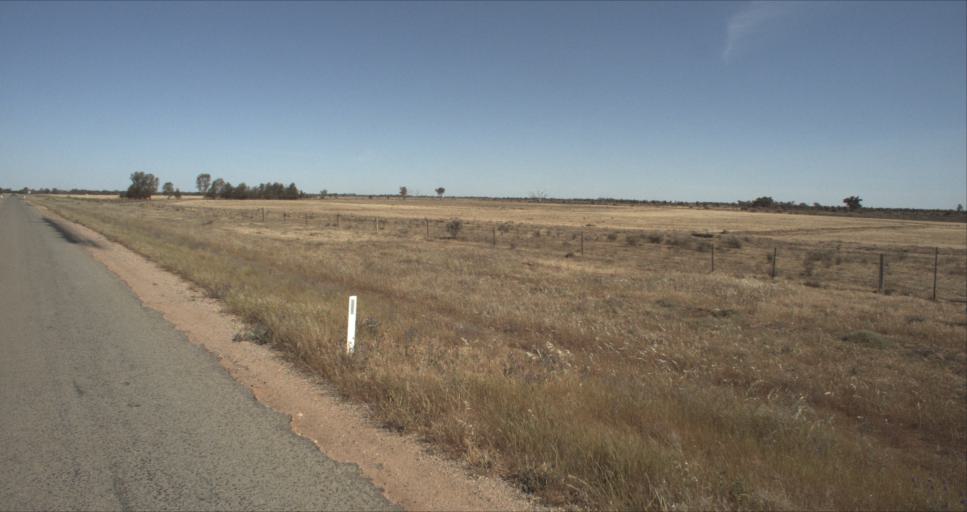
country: AU
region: New South Wales
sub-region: Leeton
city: Leeton
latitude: -34.4882
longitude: 146.3799
